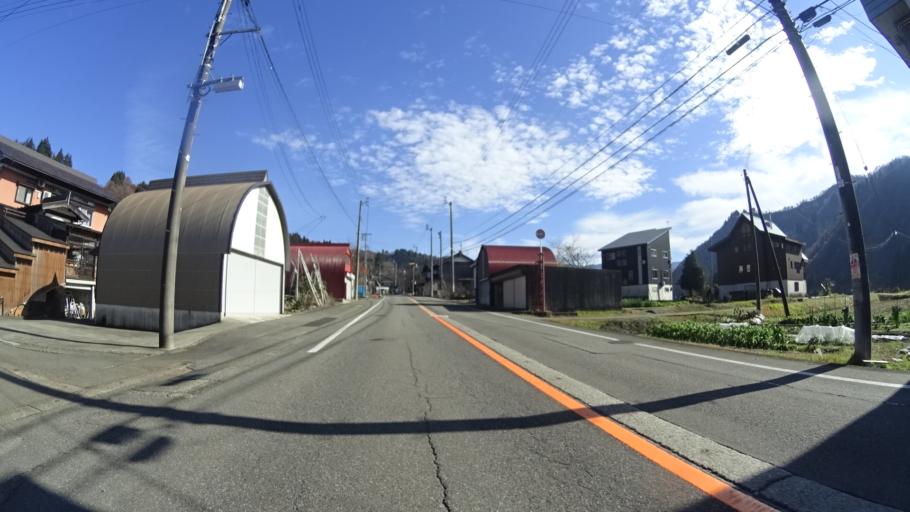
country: JP
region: Niigata
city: Muikamachi
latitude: 37.2122
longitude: 139.0486
